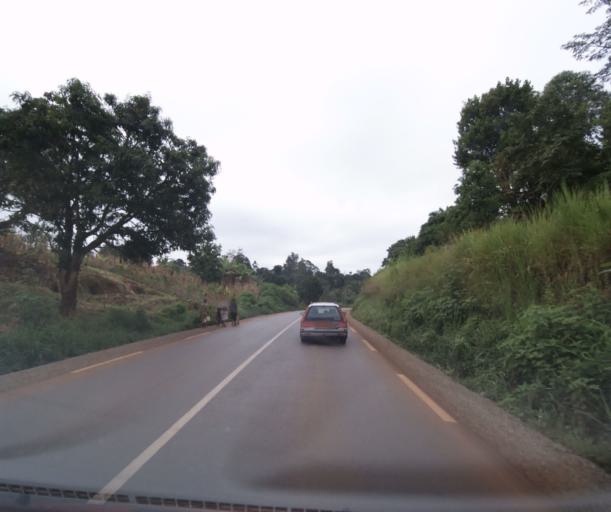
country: CM
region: West
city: Mbouda
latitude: 5.5732
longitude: 10.3090
